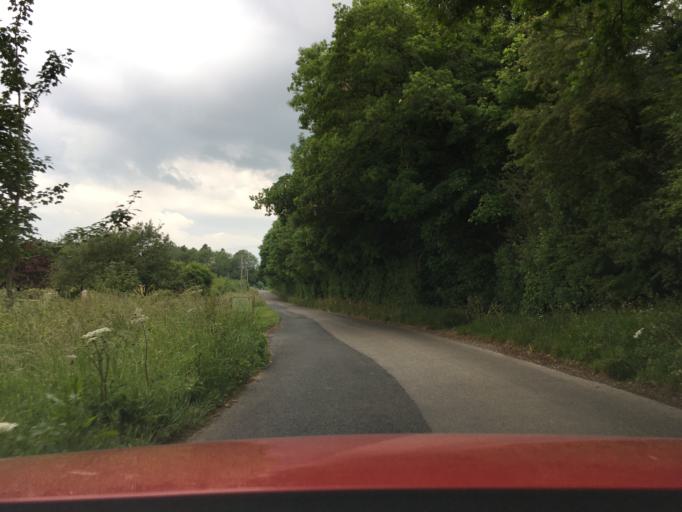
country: GB
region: England
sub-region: Gloucestershire
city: Coates
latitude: 51.7495
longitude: -2.0547
